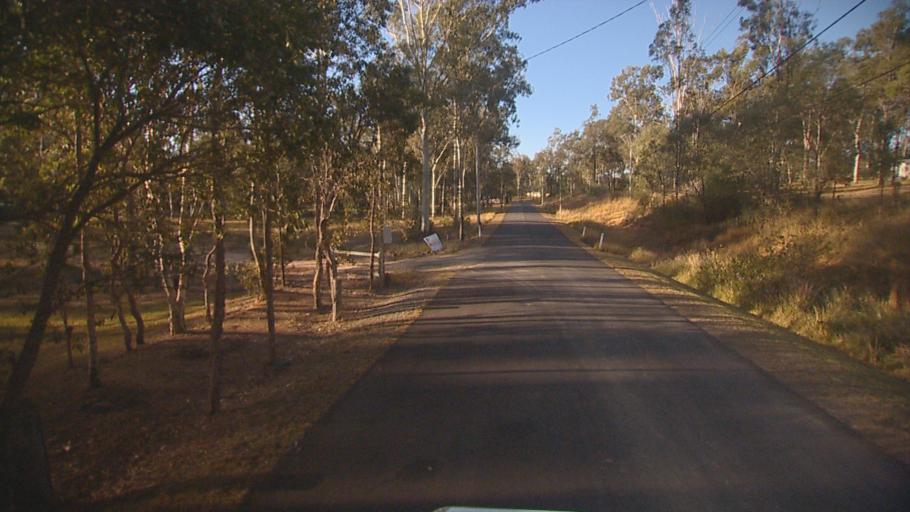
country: AU
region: Queensland
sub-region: Logan
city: Cedar Vale
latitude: -27.8555
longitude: 153.0938
